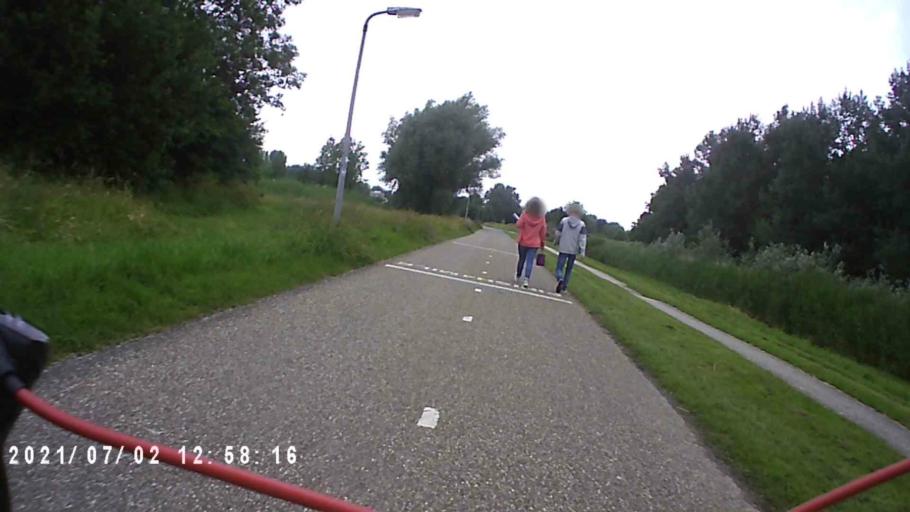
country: NL
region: Groningen
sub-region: Gemeente Groningen
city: Oosterpark
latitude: 53.2420
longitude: 6.6009
